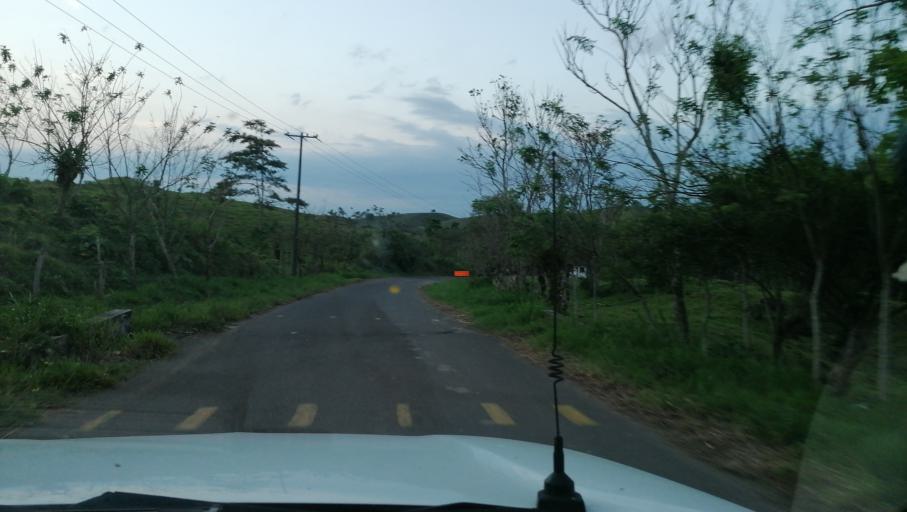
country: MX
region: Chiapas
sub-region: Ostuacan
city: Nuevo Juan del Grijalva
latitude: 17.4409
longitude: -93.3514
